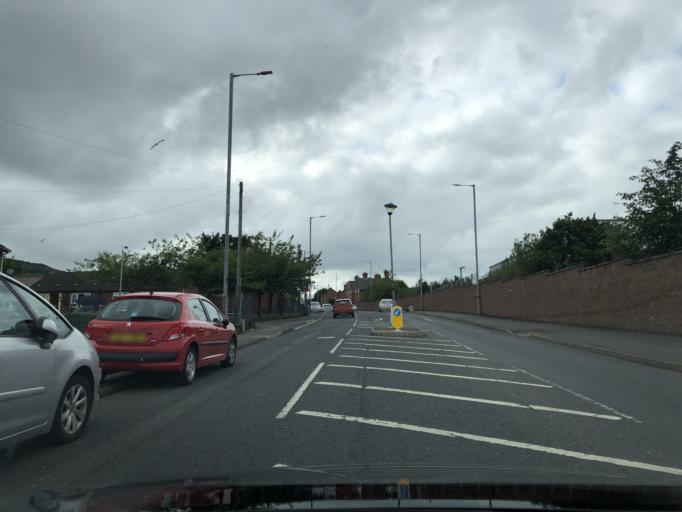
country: GB
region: Northern Ireland
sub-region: Newtownabbey District
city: Newtownabbey
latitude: 54.6523
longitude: -5.9191
